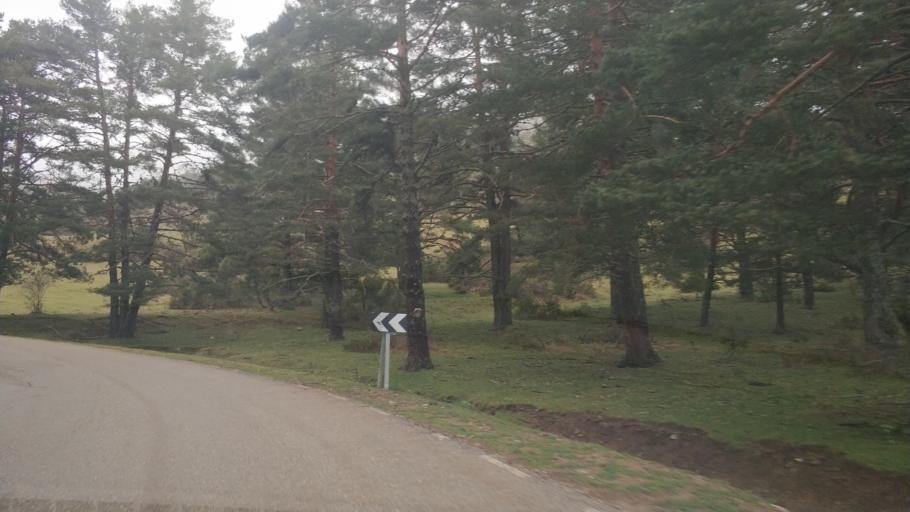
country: ES
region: Castille and Leon
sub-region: Provincia de Burgos
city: Neila
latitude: 42.0356
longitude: -3.0049
